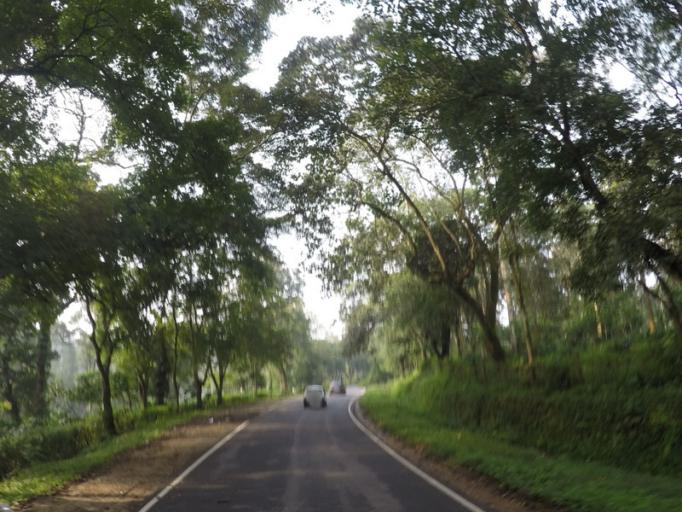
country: IN
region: Karnataka
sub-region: Chikmagalur
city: Mudigere
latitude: 13.2634
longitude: 75.6262
